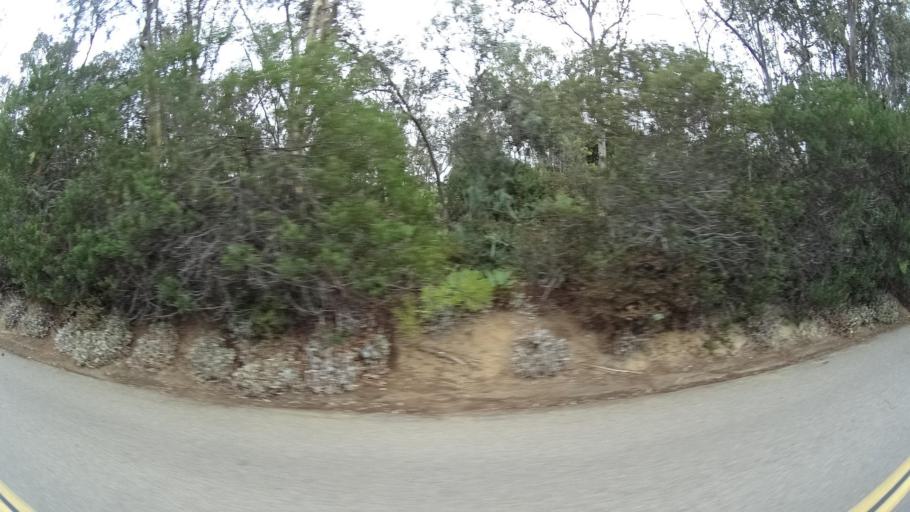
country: US
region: California
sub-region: San Diego County
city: Solana Beach
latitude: 32.9949
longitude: -117.2341
